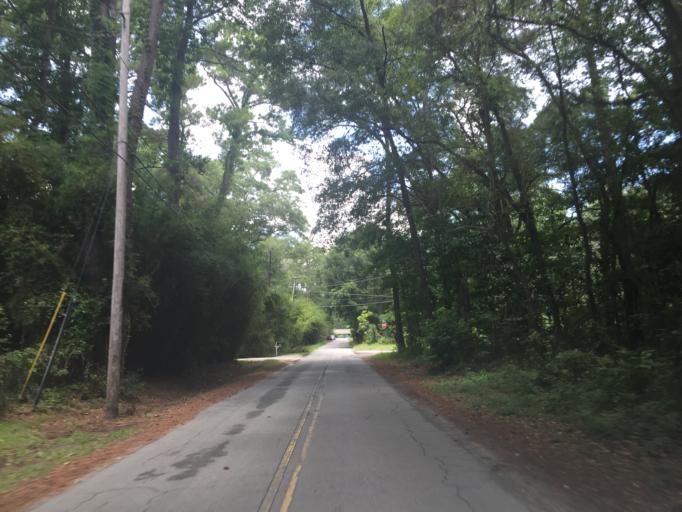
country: US
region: Georgia
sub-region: Chatham County
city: Montgomery
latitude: 31.9529
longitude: -81.0986
